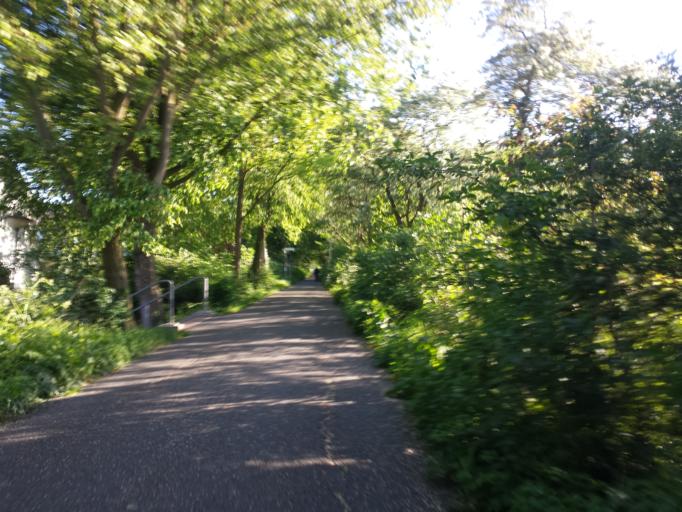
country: DE
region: Lower Saxony
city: Lilienthal
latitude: 53.1065
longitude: 8.8690
